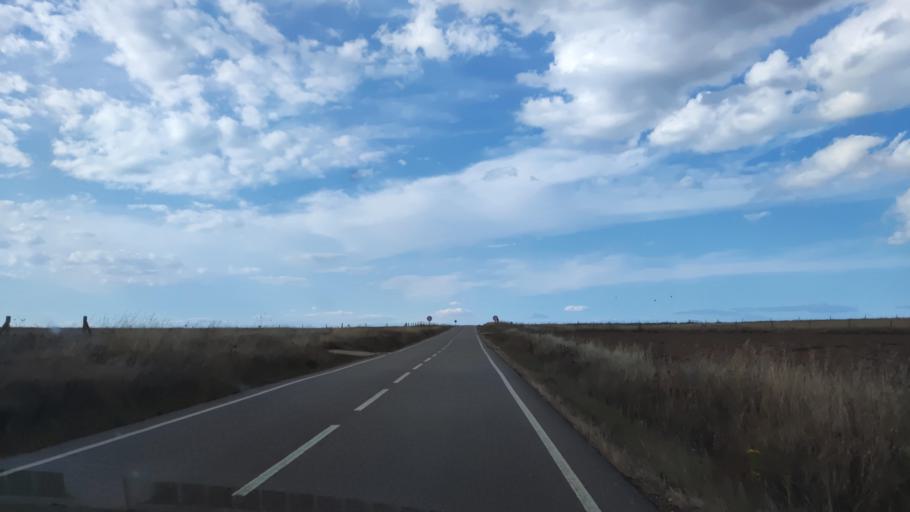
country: ES
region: Castille and Leon
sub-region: Provincia de Salamanca
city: Pastores
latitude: 40.5089
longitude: -6.5048
